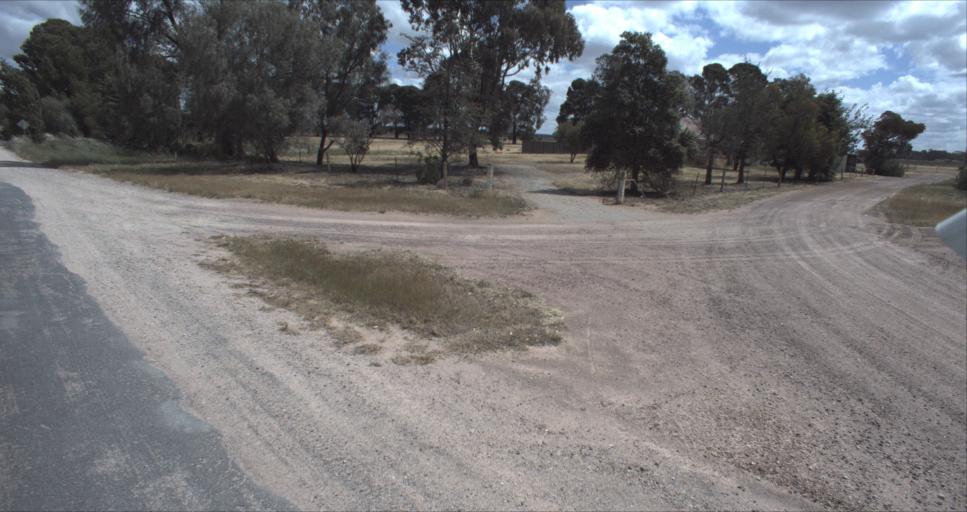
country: AU
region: New South Wales
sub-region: Leeton
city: Leeton
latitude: -34.5885
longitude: 146.3611
